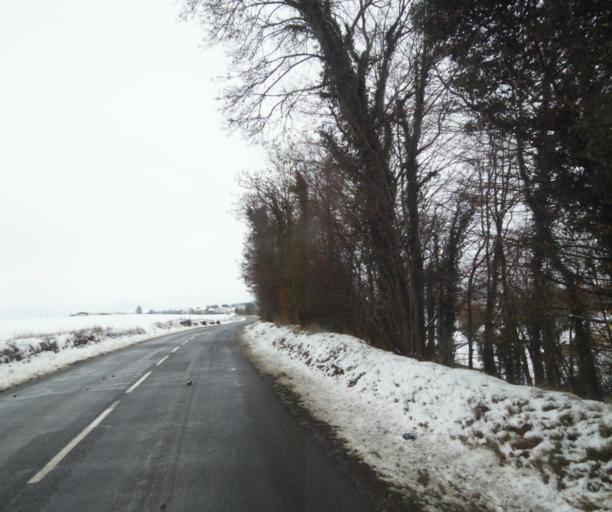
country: FR
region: Champagne-Ardenne
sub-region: Departement de la Haute-Marne
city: Wassy
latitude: 48.4335
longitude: 4.9617
